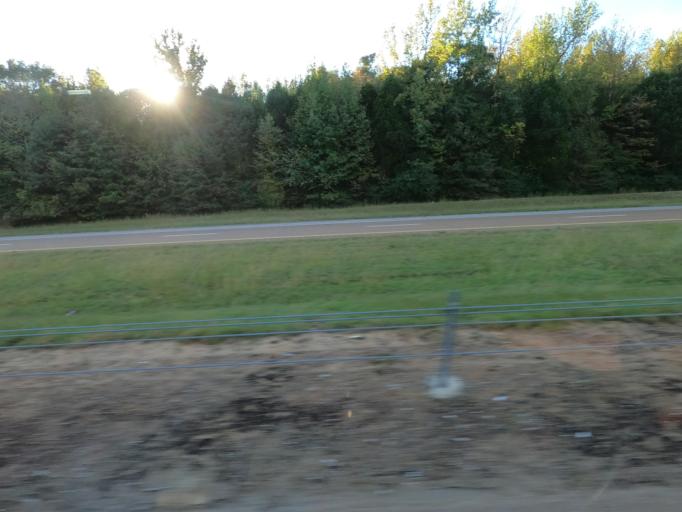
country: US
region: Tennessee
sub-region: Shelby County
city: Arlington
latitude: 35.2670
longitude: -89.6787
